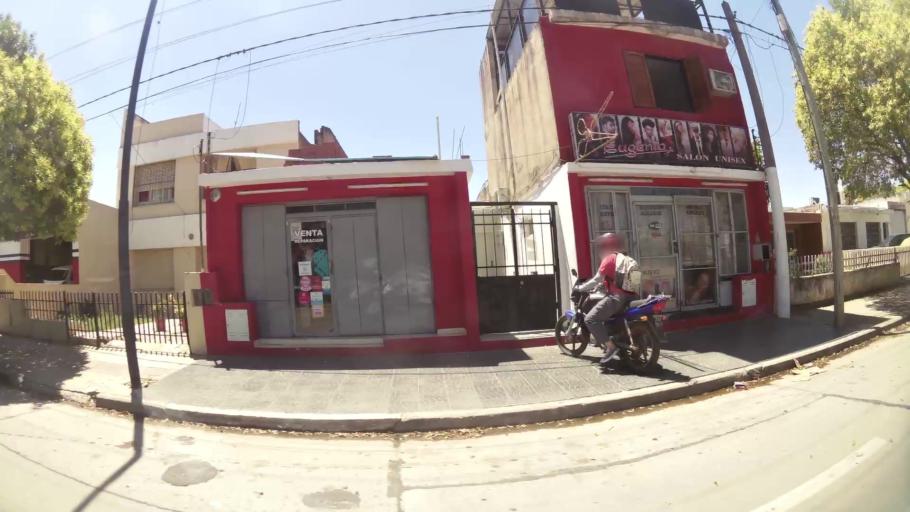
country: AR
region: Cordoba
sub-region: Departamento de Capital
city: Cordoba
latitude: -31.3783
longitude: -64.1377
